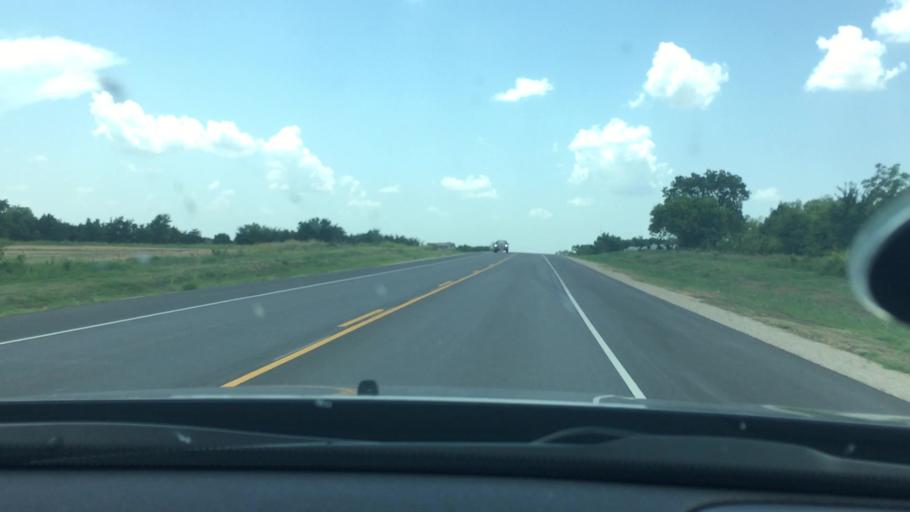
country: US
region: Oklahoma
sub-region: Johnston County
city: Tishomingo
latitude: 34.3344
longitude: -96.6516
